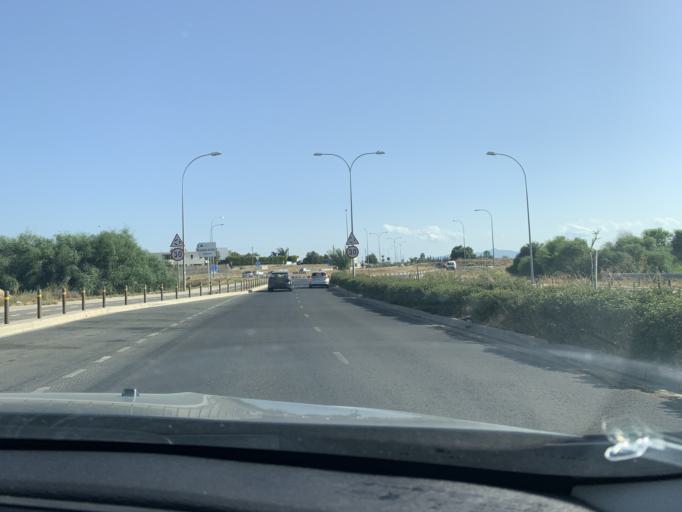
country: CY
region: Lefkosia
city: Tseri
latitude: 35.1166
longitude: 33.3564
